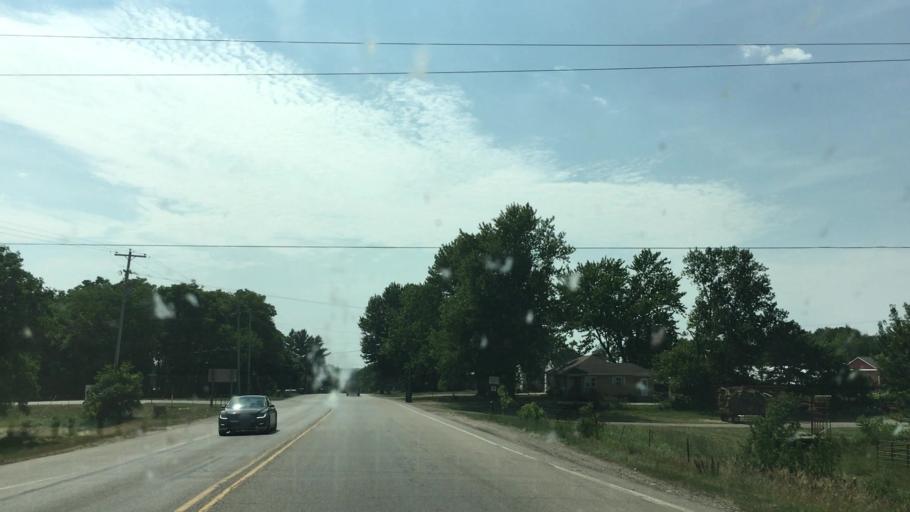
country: US
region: Michigan
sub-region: Kent County
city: Cutlerville
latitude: 42.7827
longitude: -85.6695
